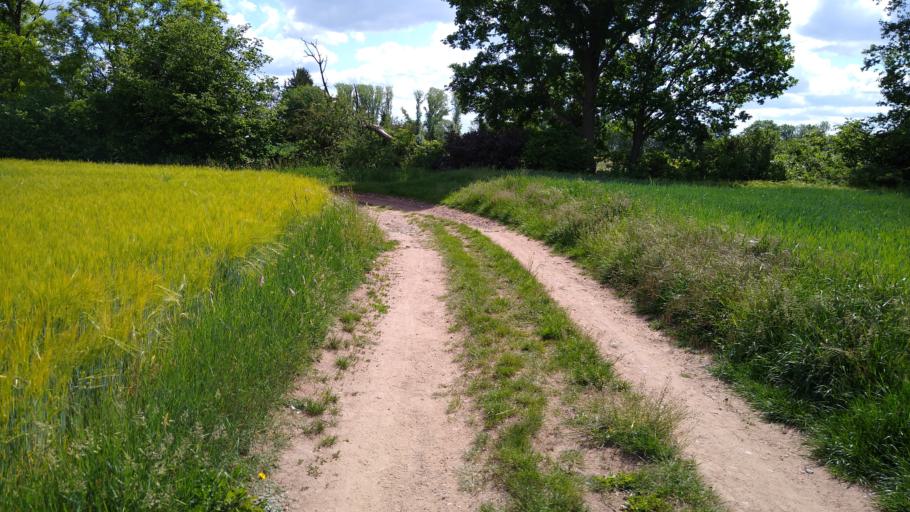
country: DE
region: Bavaria
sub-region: Regierungsbezirk Mittelfranken
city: Seukendorf
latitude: 49.4816
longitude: 10.9209
